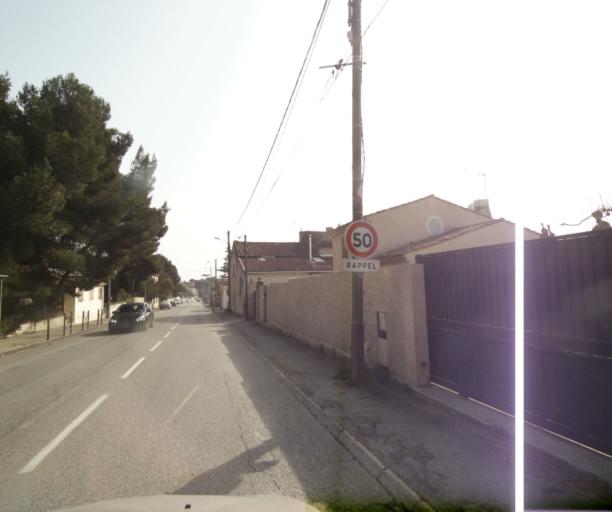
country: FR
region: Provence-Alpes-Cote d'Azur
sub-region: Departement des Bouches-du-Rhone
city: Marseille 15
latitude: 43.3901
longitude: 5.3442
